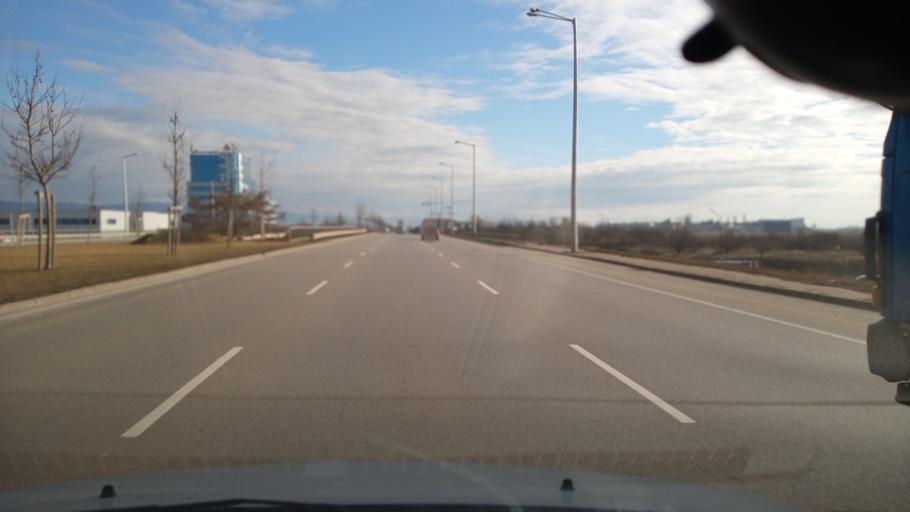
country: BG
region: Sofia-Capital
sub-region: Stolichna Obshtina
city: Sofia
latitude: 42.7037
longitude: 23.3908
